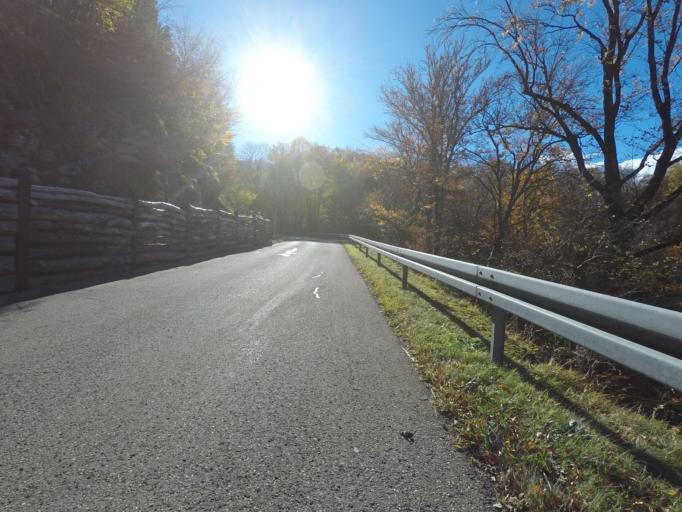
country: DE
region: Baden-Wuerttemberg
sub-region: Tuebingen Region
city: Pfullingen
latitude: 48.4140
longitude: 9.2365
